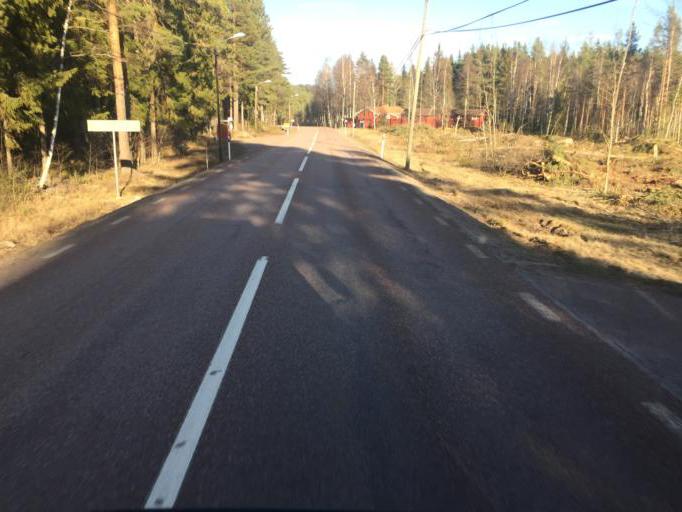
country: SE
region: Dalarna
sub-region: Gagnefs Kommun
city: Mockfjard
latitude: 60.5071
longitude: 14.8371
